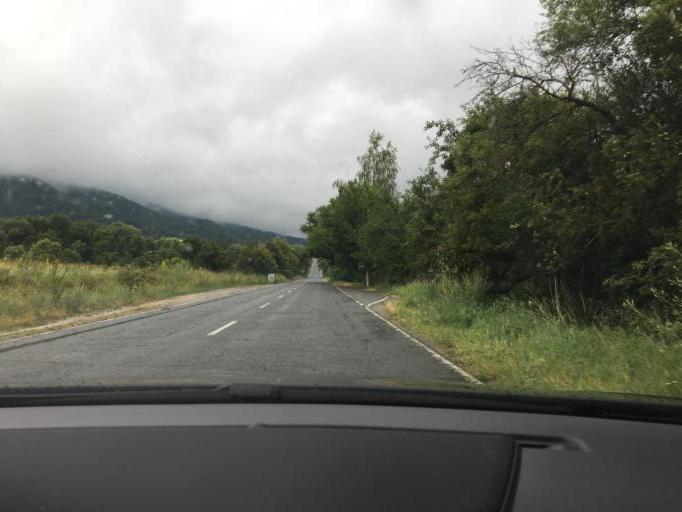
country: BG
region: Kyustendil
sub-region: Obshtina Kyustendil
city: Kyustendil
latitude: 42.2446
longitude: 22.5185
